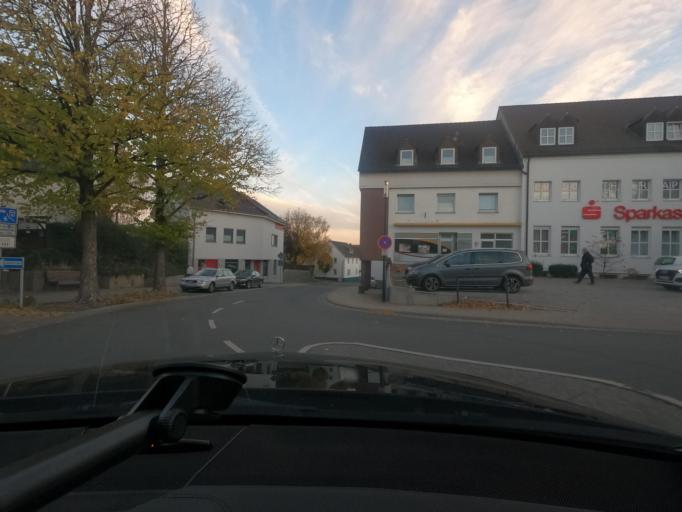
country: DE
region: North Rhine-Westphalia
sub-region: Regierungsbezirk Arnsberg
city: Mohnesee
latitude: 51.4966
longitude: 8.1296
